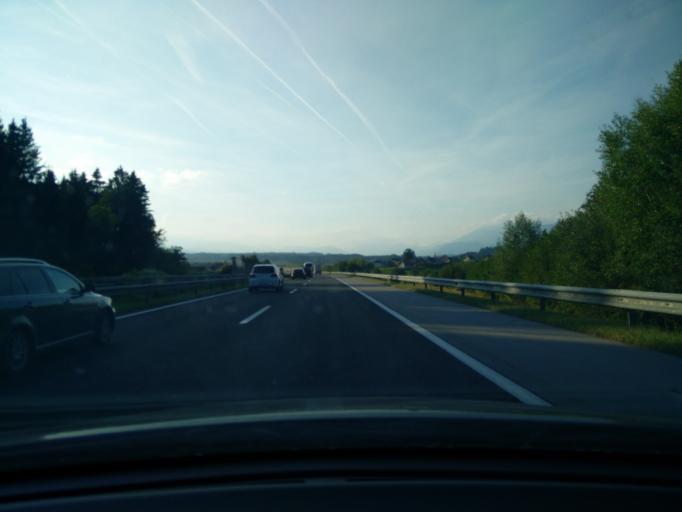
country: SI
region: Naklo
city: Naklo
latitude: 46.2724
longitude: 14.3264
